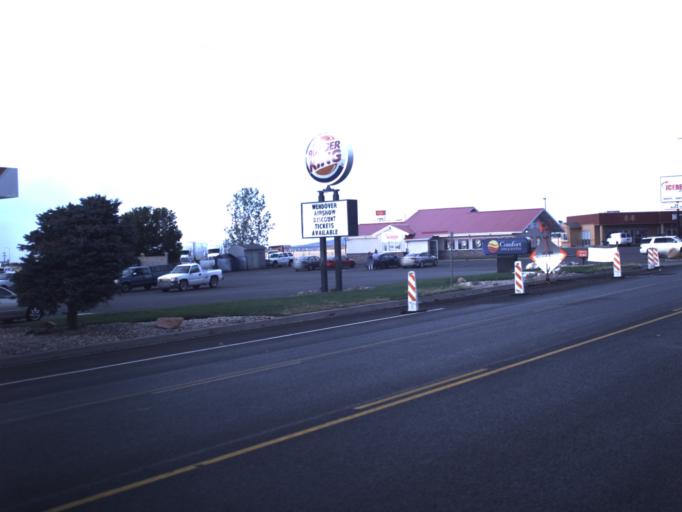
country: US
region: Utah
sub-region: Millard County
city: Fillmore
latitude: 38.9486
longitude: -112.3462
